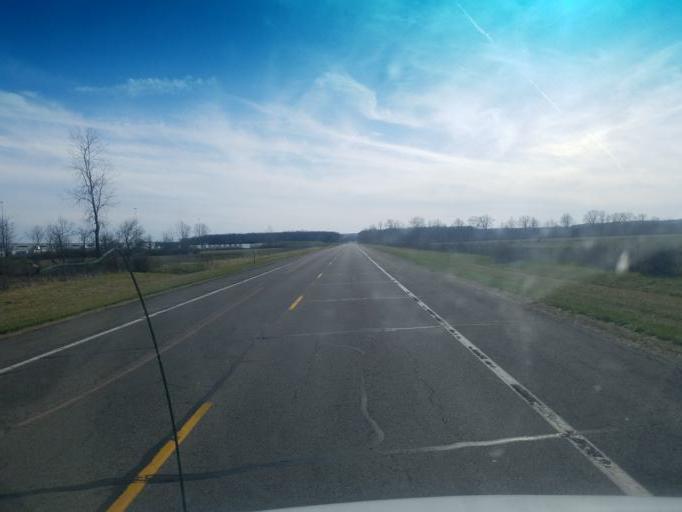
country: US
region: Ohio
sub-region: Champaign County
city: North Lewisburg
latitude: 40.3367
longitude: -83.5496
